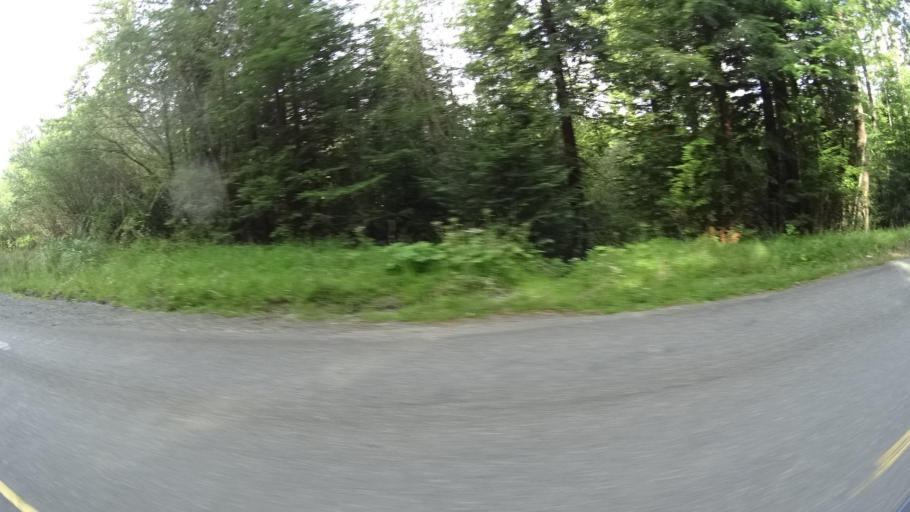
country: US
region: California
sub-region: Humboldt County
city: Bayside
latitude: 40.7572
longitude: -124.0048
